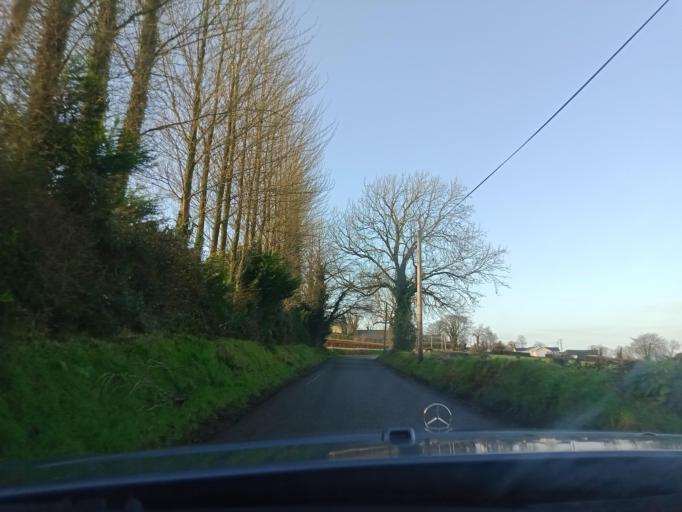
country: IE
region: Leinster
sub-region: Kilkenny
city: Callan
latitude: 52.4669
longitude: -7.4051
